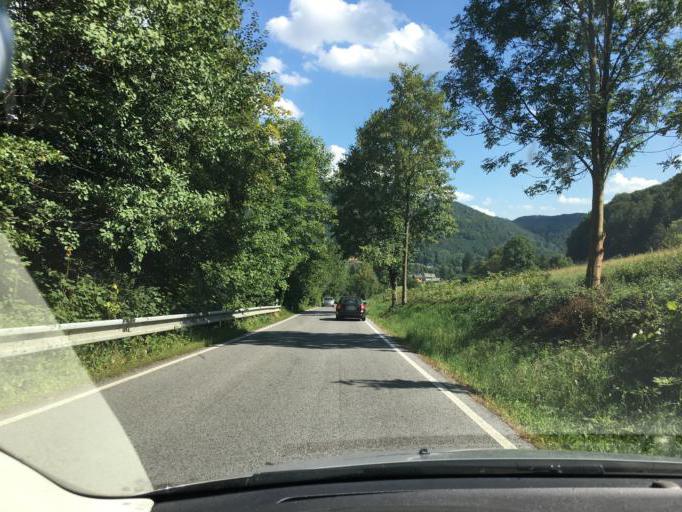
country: CZ
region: Liberecky
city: Mala Skala
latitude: 50.6414
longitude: 15.1815
